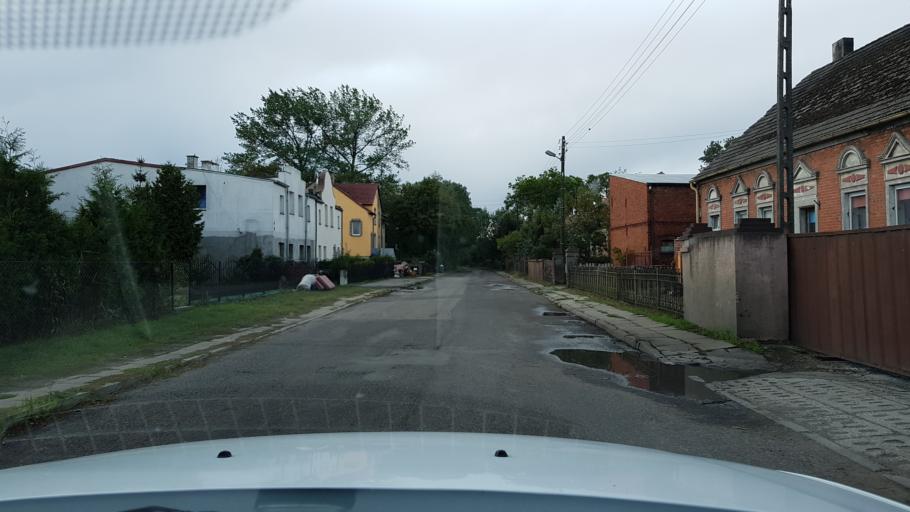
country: PL
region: West Pomeranian Voivodeship
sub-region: Powiat gryfinski
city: Gryfino
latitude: 53.2845
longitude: 14.4995
